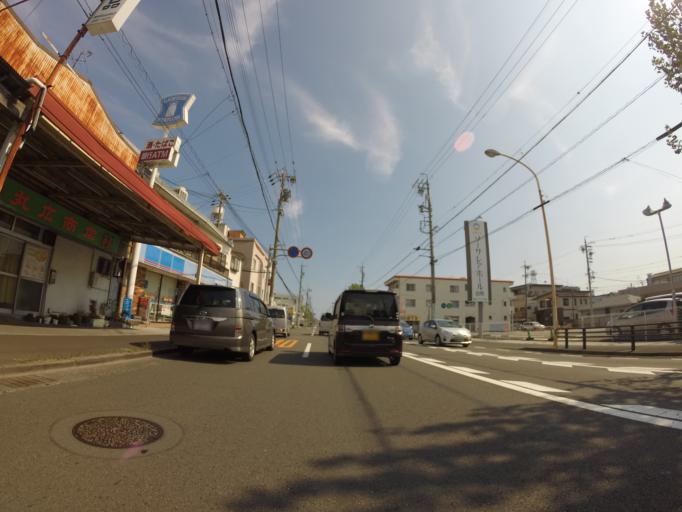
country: JP
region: Shizuoka
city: Shizuoka-shi
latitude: 34.9707
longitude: 138.3689
